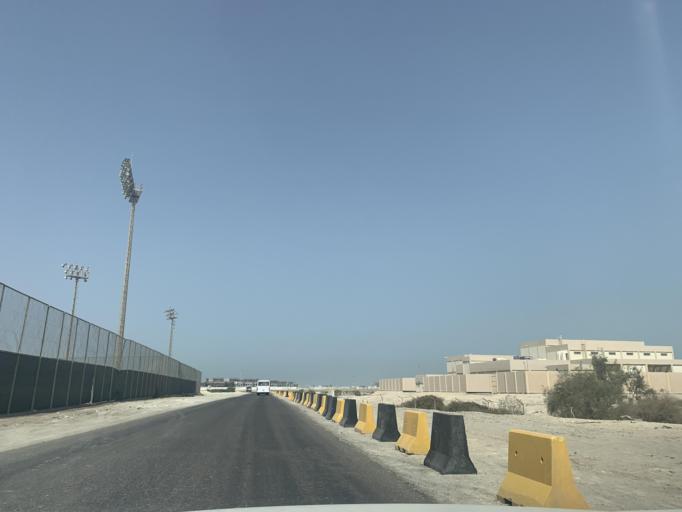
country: BH
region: Northern
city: Sitrah
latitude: 26.1554
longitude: 50.6262
